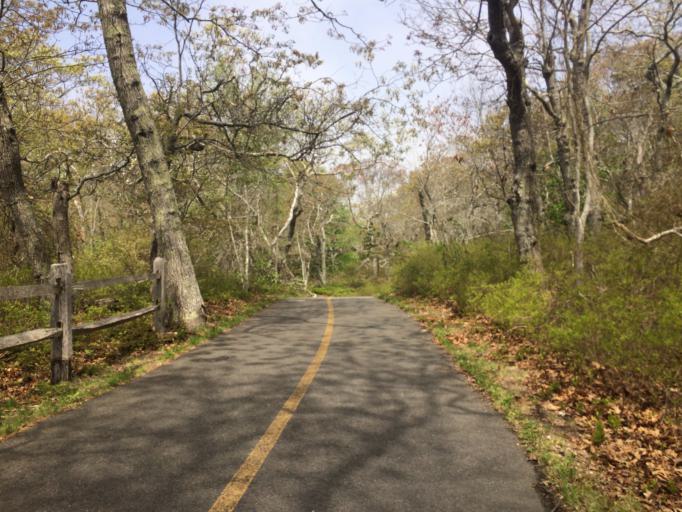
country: US
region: Massachusetts
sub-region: Barnstable County
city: Provincetown
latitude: 42.0701
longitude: -70.1959
